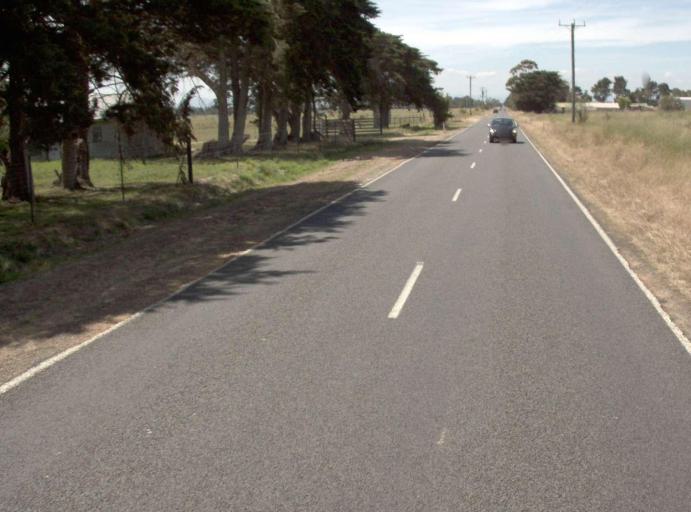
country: AU
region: Victoria
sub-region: Wellington
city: Heyfield
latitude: -38.0871
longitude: 146.8672
